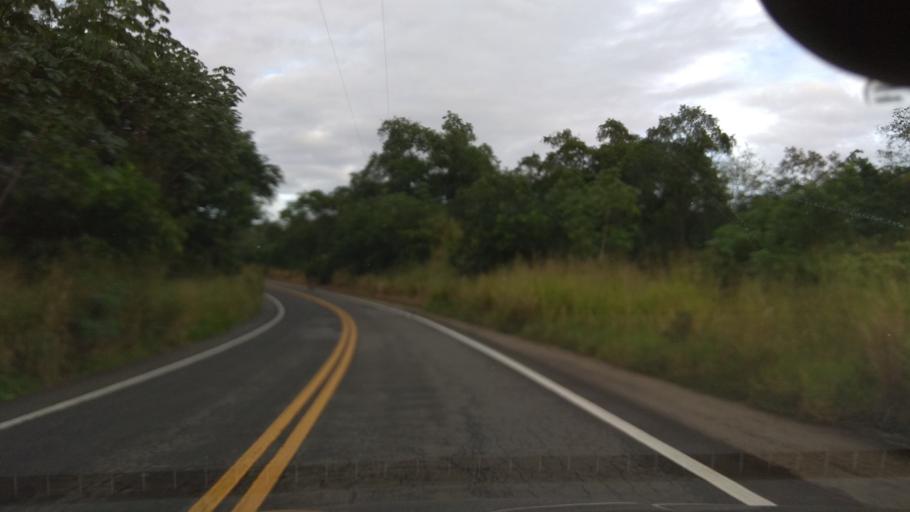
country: BR
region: Bahia
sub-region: Ubaitaba
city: Ubaitaba
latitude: -14.2580
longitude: -39.3526
